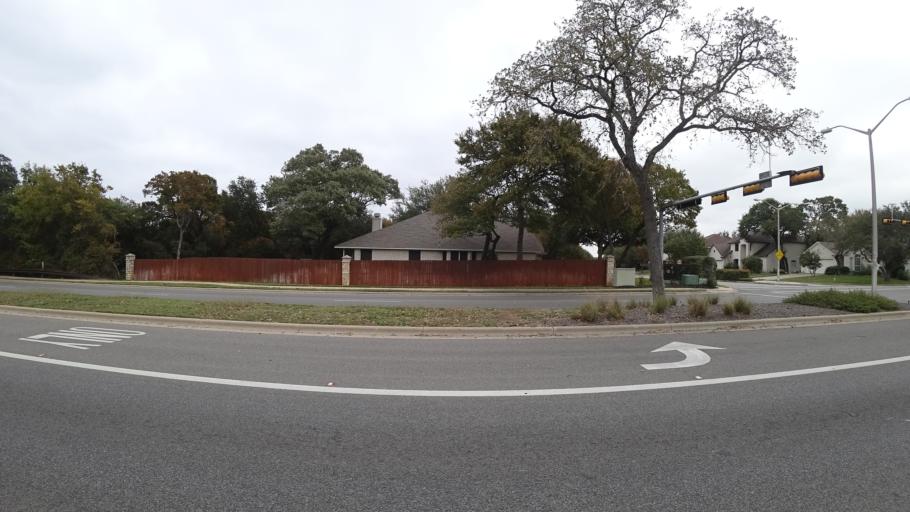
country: US
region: Texas
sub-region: Williamson County
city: Cedar Park
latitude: 30.4886
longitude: -97.8381
